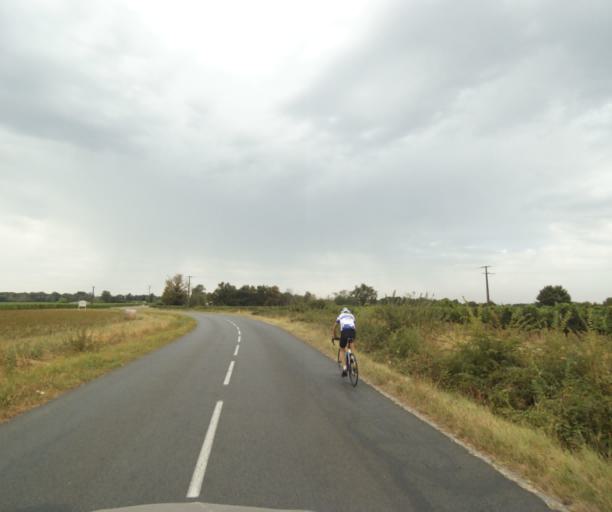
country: FR
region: Aquitaine
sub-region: Departement de la Gironde
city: Creon
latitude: 44.7688
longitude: -0.3350
